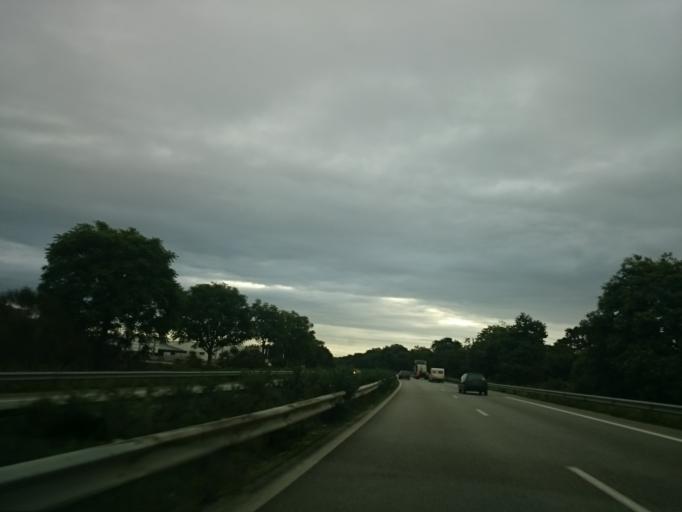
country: FR
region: Brittany
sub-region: Departement du Finistere
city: Ergue-Gaberic
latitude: 47.9723
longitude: -4.0040
